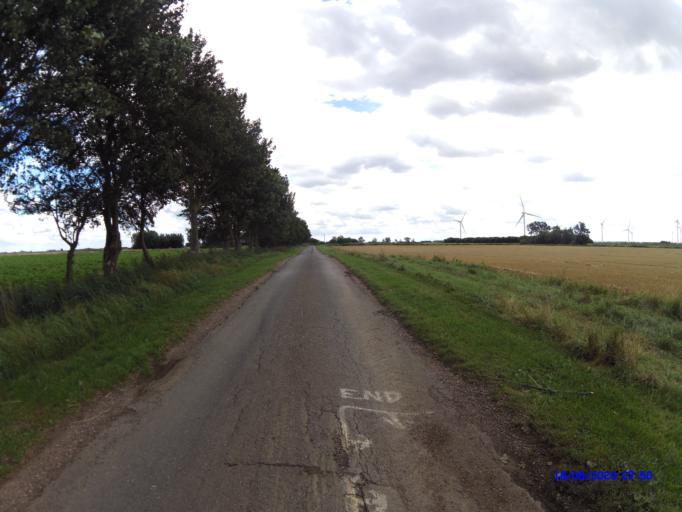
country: GB
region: England
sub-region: Cambridgeshire
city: Whittlesey
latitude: 52.5200
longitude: -0.0942
